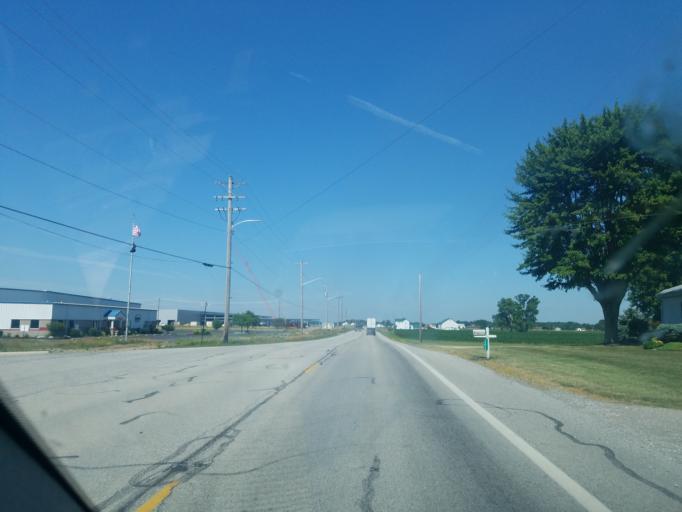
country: US
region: Ohio
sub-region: Shelby County
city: Jackson Center
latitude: 40.4398
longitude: -84.0570
